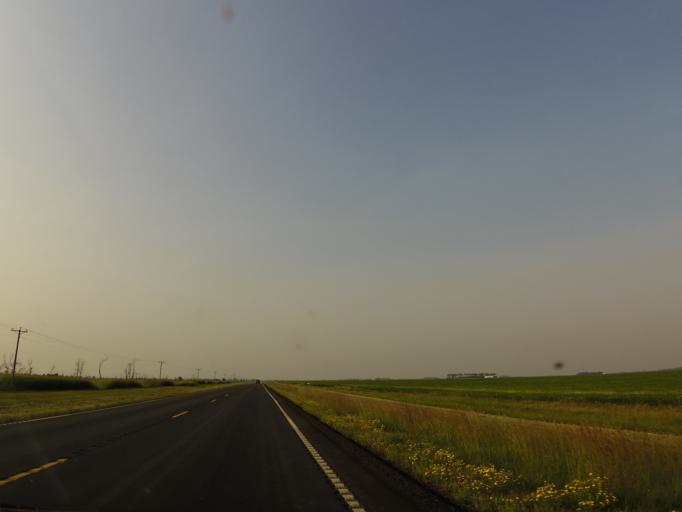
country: US
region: North Dakota
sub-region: Traill County
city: Mayville
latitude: 47.3980
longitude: -97.3261
